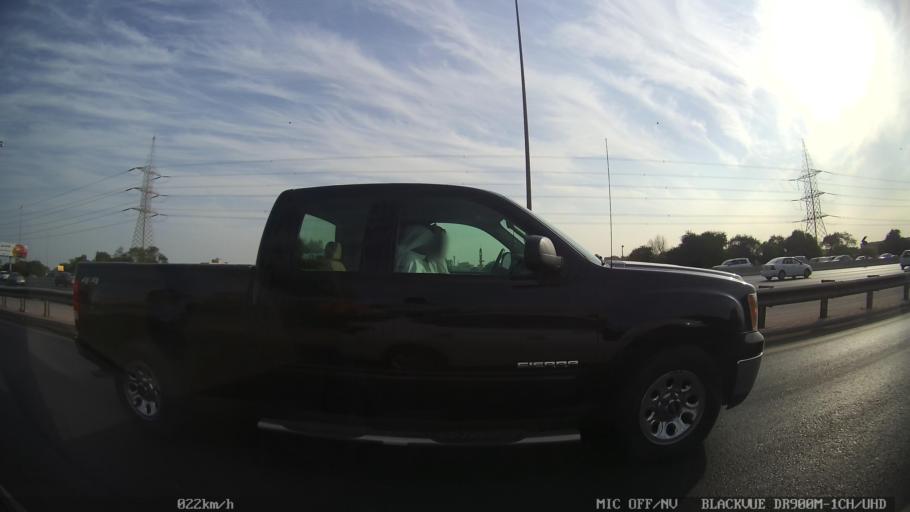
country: KW
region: Al Farwaniyah
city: Al Farwaniyah
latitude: 29.3042
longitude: 47.9739
